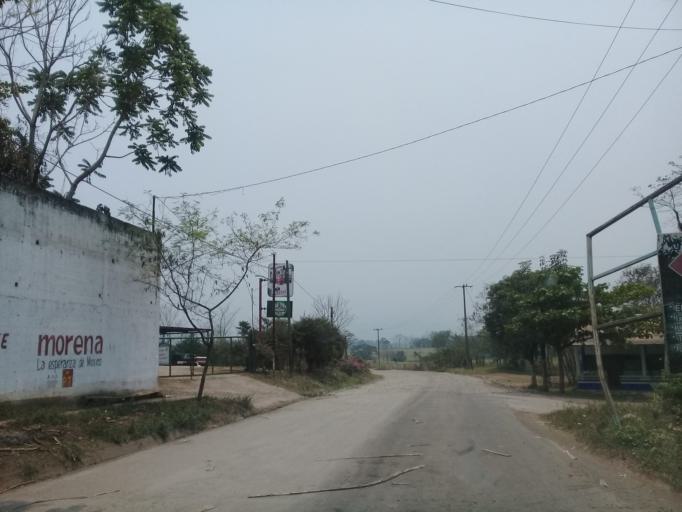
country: MX
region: Veracruz
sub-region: Tezonapa
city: Laguna Chica (Pueblo Nuevo)
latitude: 18.5429
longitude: -96.7370
